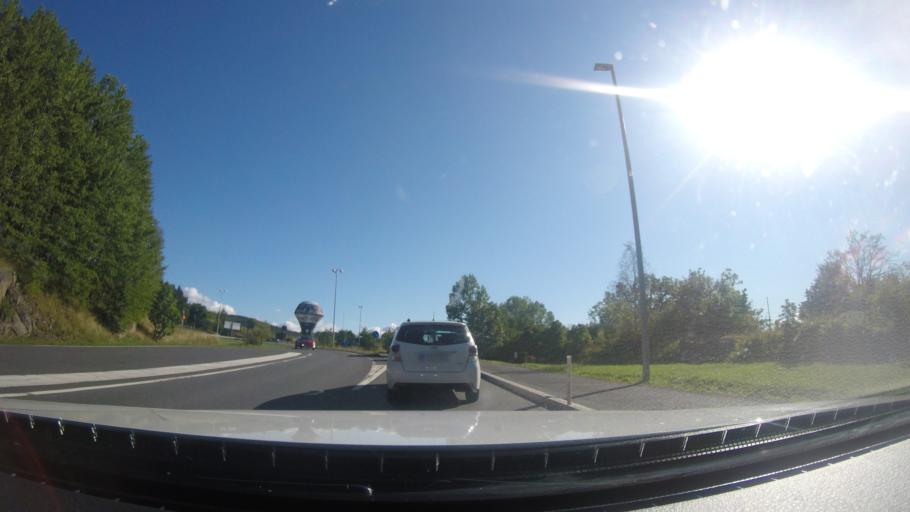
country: SE
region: Joenkoeping
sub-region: Jonkopings Kommun
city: Graenna
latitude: 58.0038
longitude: 14.4522
